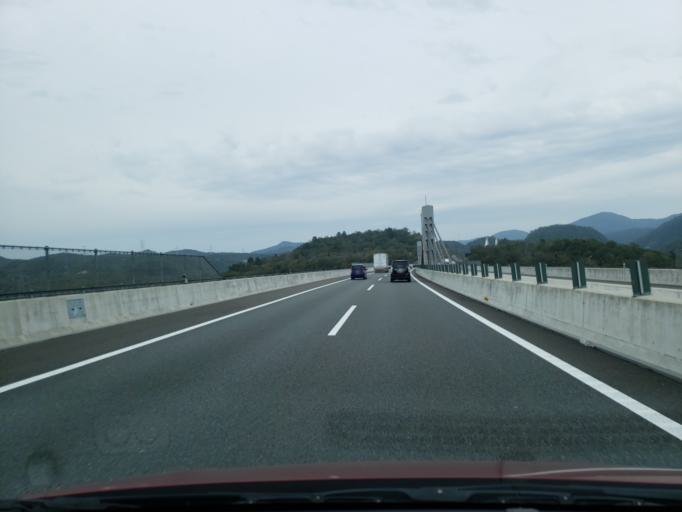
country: JP
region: Hyogo
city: Sandacho
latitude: 34.8646
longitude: 135.2645
